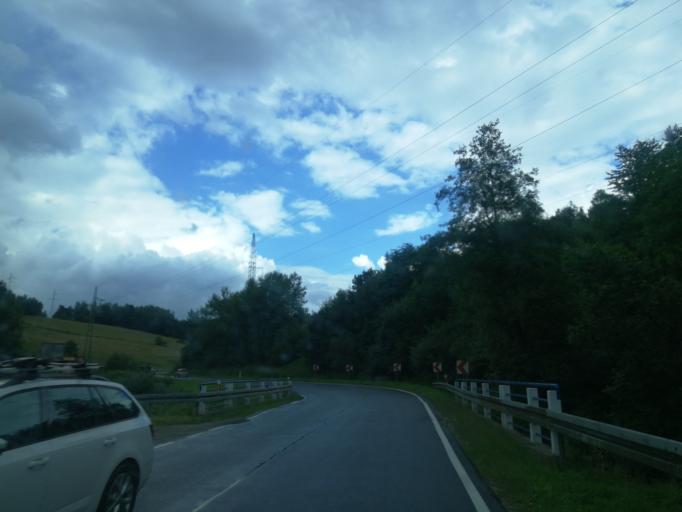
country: PL
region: Subcarpathian Voivodeship
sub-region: Powiat leski
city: Olszanica
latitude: 49.4251
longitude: 22.4533
